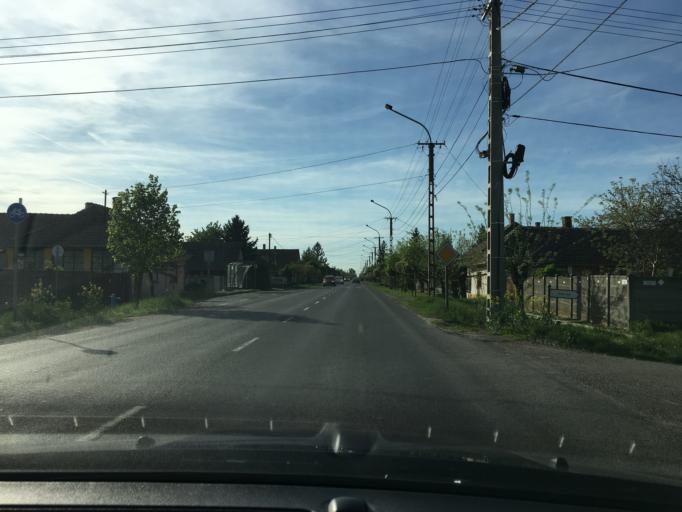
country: HU
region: Bekes
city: Korostarcsa
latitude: 46.8717
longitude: 21.0258
